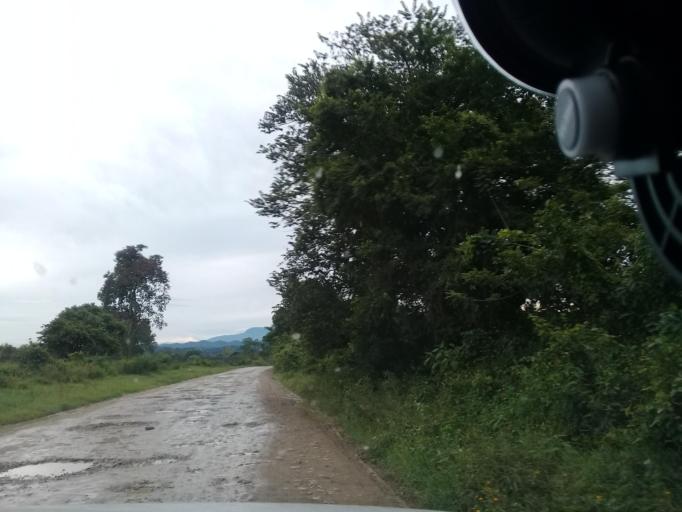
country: MX
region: Hidalgo
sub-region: Huejutla de Reyes
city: Chalahuiyapa
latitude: 21.1598
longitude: -98.3667
